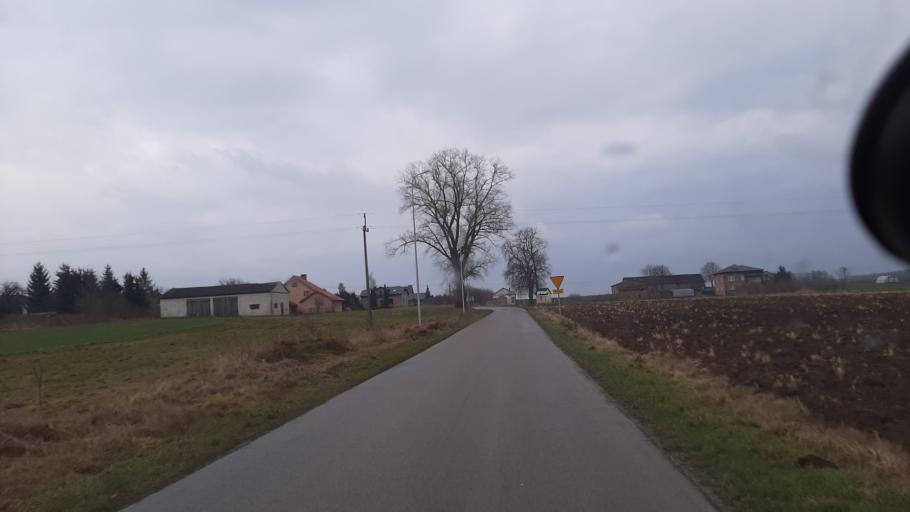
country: PL
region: Lublin Voivodeship
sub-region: Powiat lubelski
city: Jastkow
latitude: 51.3619
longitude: 22.4555
